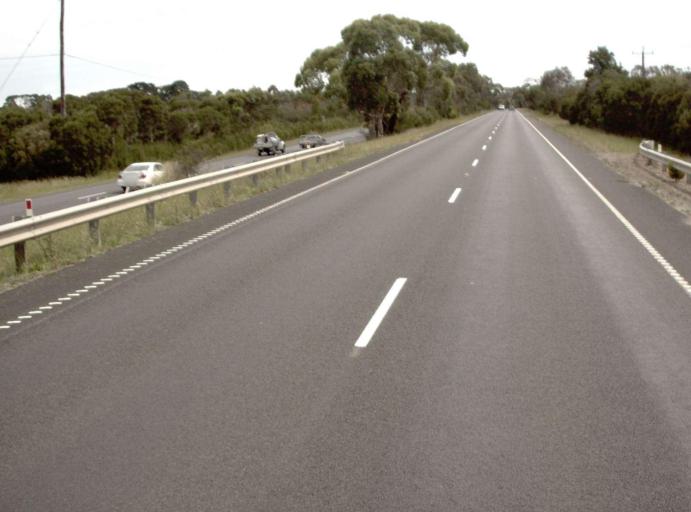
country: AU
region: Victoria
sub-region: Mornington Peninsula
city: Moorooduc
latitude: -38.2069
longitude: 145.1152
